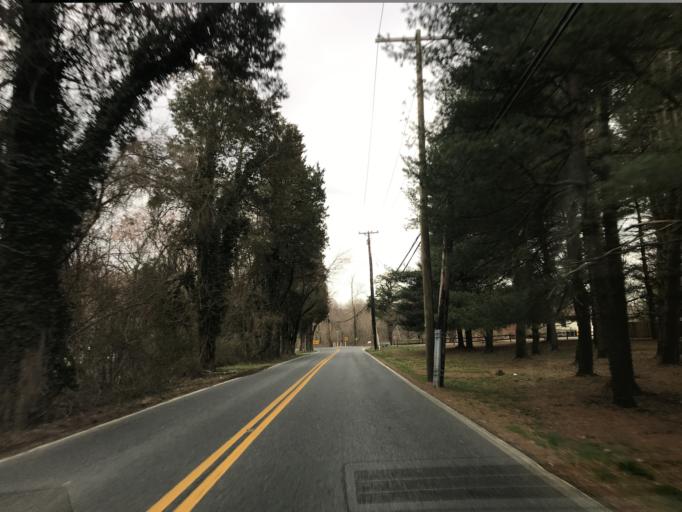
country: US
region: Maryland
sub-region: Anne Arundel County
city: Gambrills
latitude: 39.0548
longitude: -76.6352
